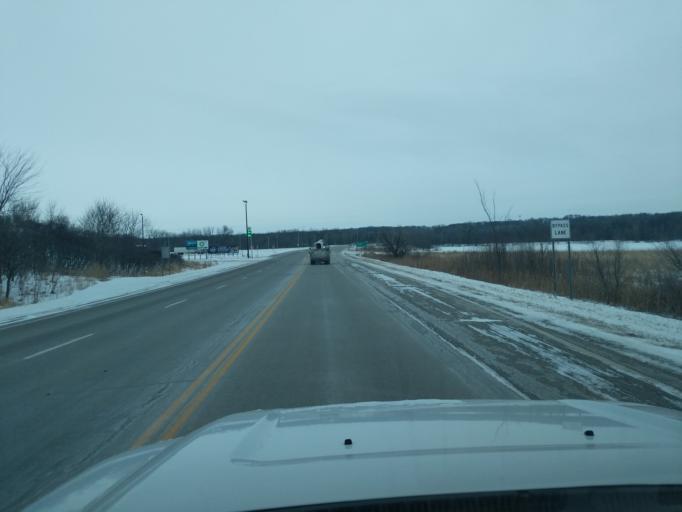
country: US
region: Minnesota
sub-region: Redwood County
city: Redwood Falls
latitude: 44.5524
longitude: -94.9962
